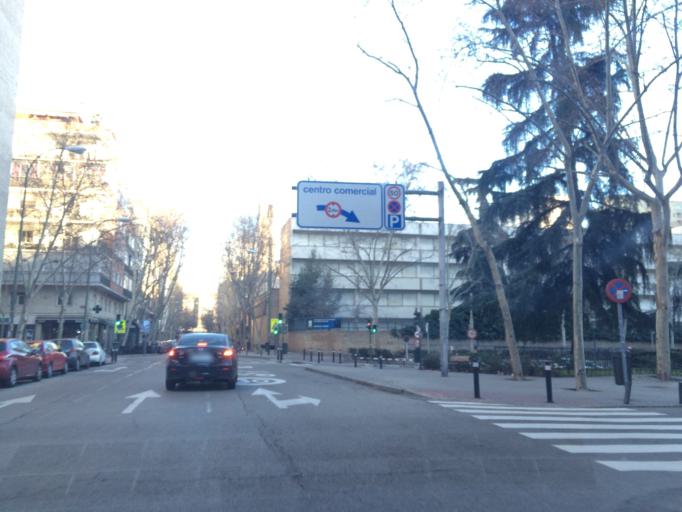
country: ES
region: Madrid
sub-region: Provincia de Madrid
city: Chamberi
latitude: 40.4490
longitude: -3.6969
